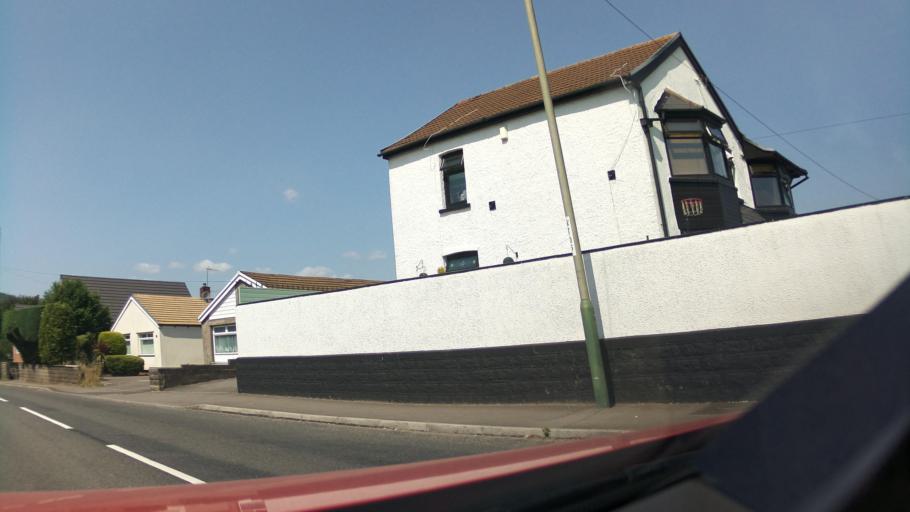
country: GB
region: Wales
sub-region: Caerphilly County Borough
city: Caerphilly
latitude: 51.5901
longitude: -3.2236
